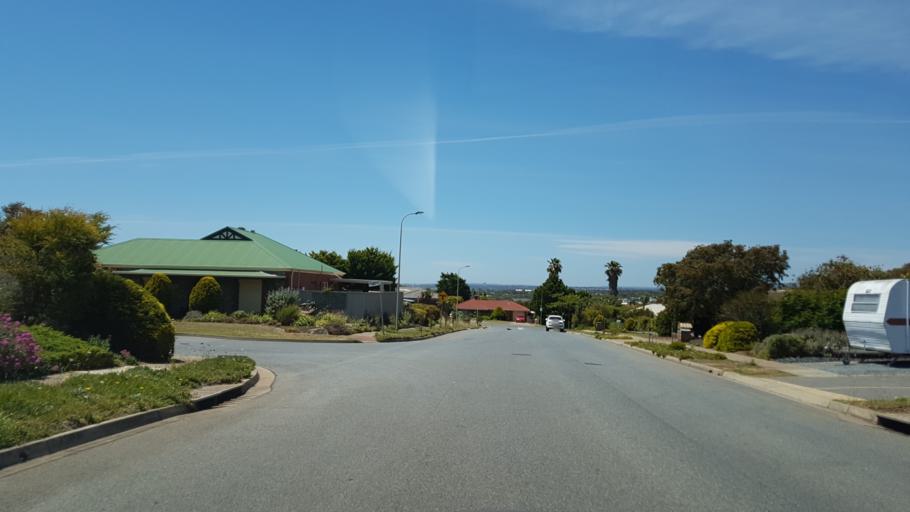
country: AU
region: South Australia
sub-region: Onkaparinga
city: Moana
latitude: -35.2146
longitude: 138.4750
